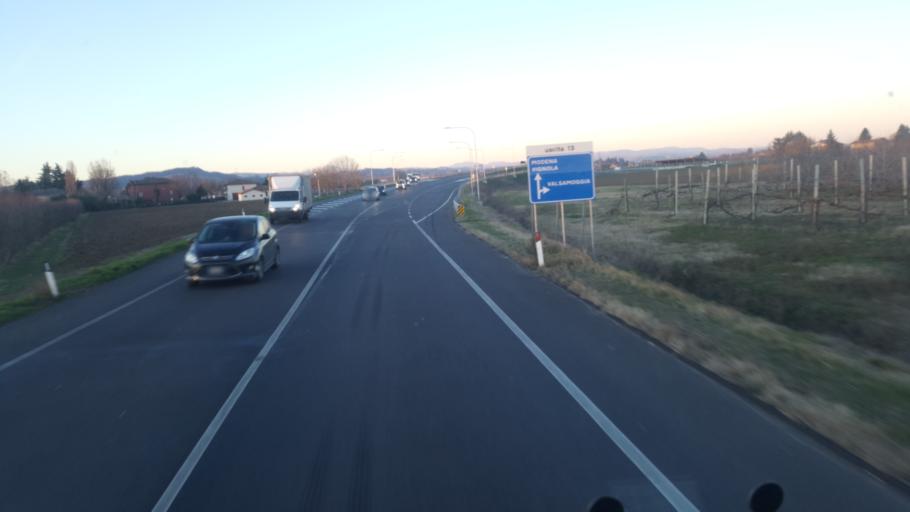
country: IT
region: Emilia-Romagna
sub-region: Provincia di Bologna
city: Crespellano
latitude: 44.5187
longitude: 11.1197
